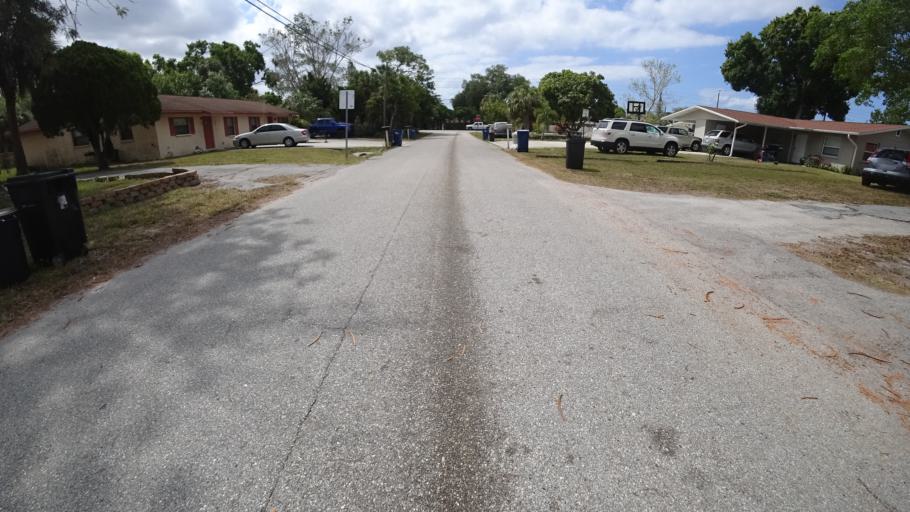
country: US
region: Florida
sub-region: Manatee County
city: Bayshore Gardens
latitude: 27.4411
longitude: -82.5830
